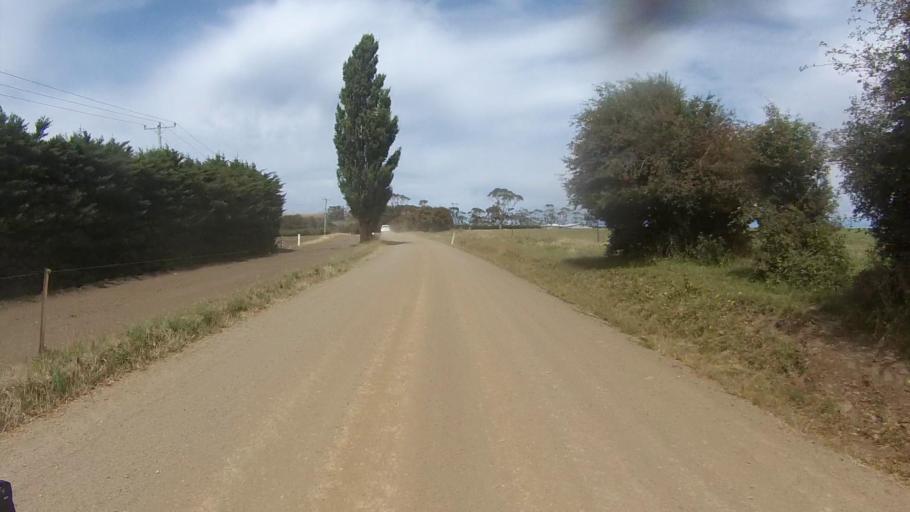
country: AU
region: Tasmania
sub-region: Sorell
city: Sorell
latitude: -42.8163
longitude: 147.8257
